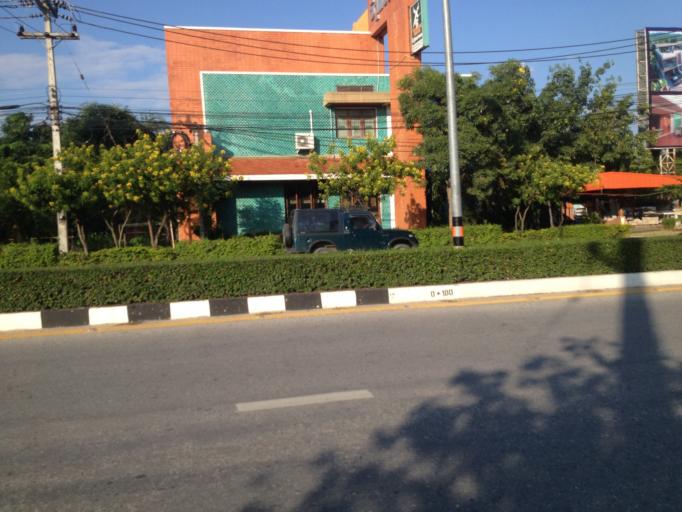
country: TH
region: Chiang Mai
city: Hang Dong
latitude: 18.7271
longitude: 98.9473
